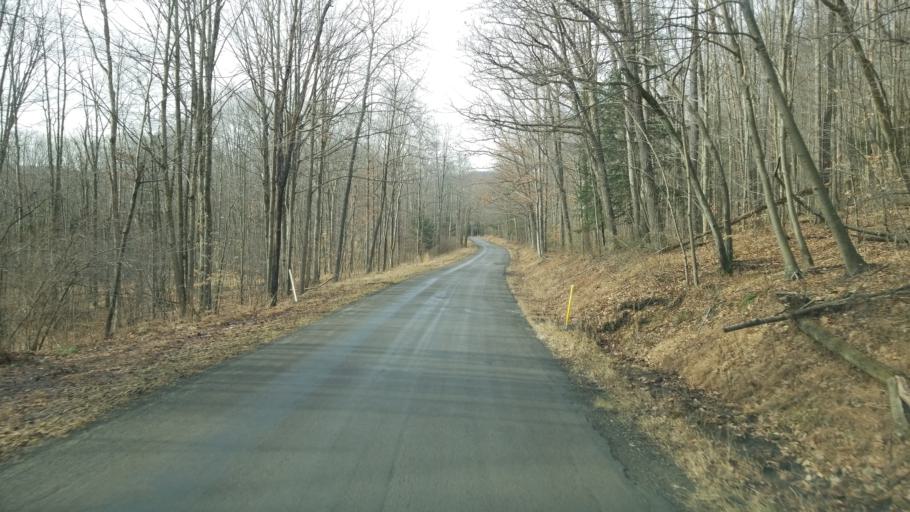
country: US
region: Pennsylvania
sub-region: Indiana County
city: Johnsonburg
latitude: 40.8328
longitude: -78.9082
